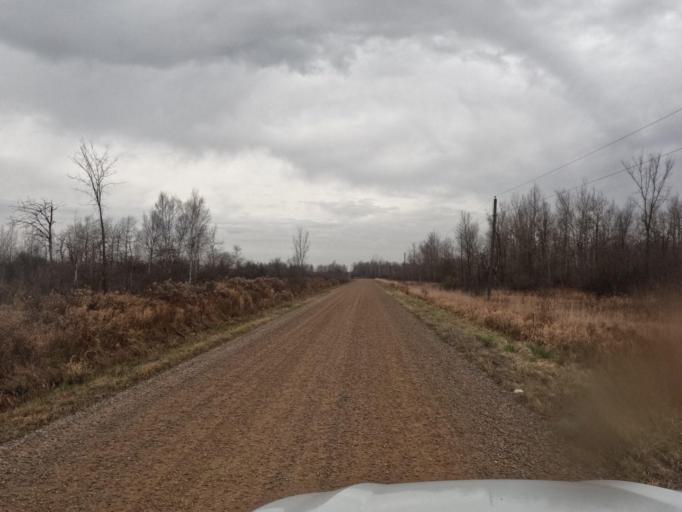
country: CA
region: Ontario
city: Shelburne
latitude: 43.8949
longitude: -80.3841
